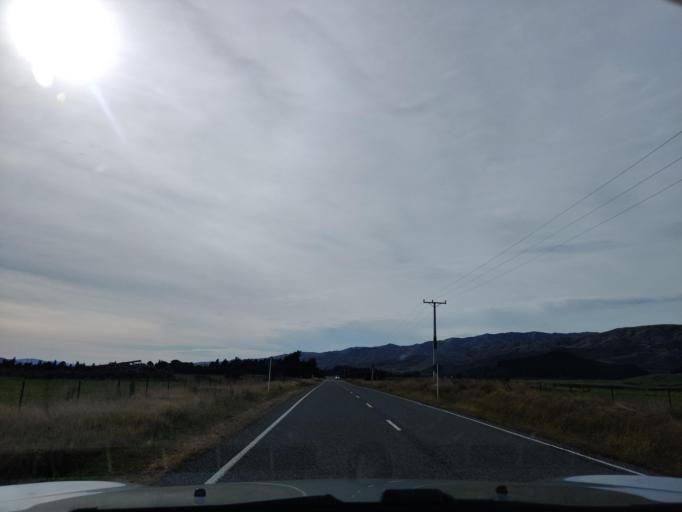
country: NZ
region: Tasman
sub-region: Tasman District
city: Brightwater
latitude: -41.6532
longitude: 173.2589
